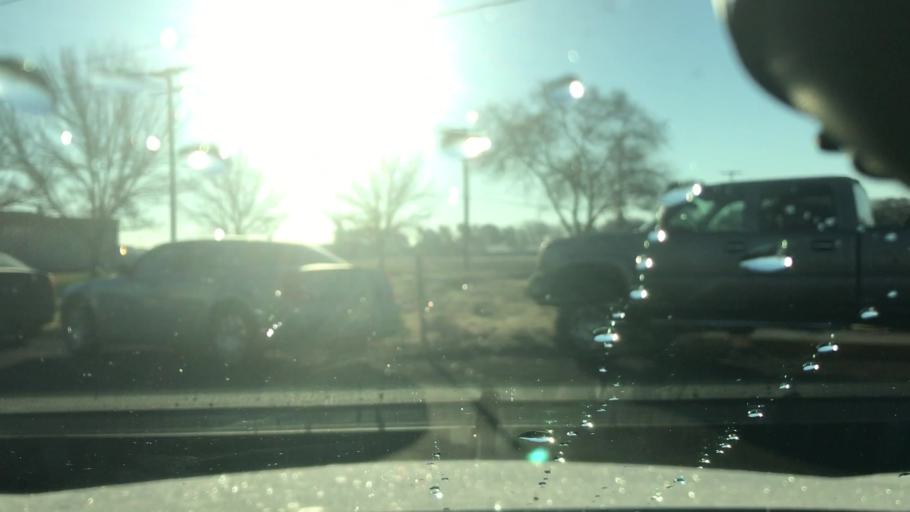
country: US
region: Washington
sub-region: Grant County
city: Moses Lake North
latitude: 47.1883
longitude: -119.3200
